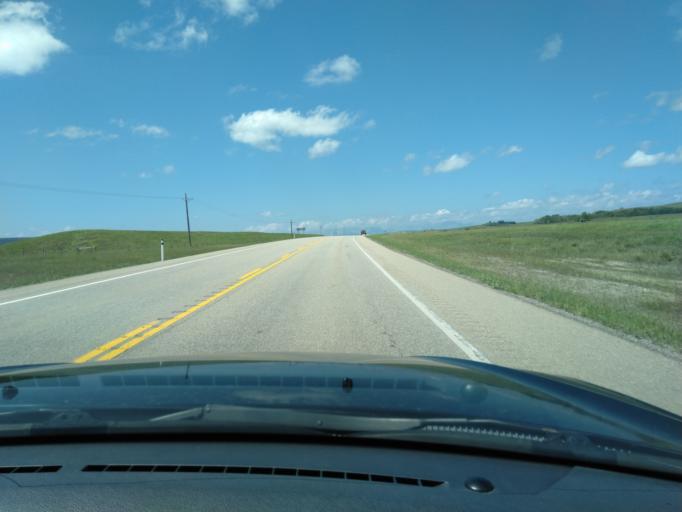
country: CA
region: Alberta
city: Cochrane
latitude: 51.2264
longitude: -114.5895
